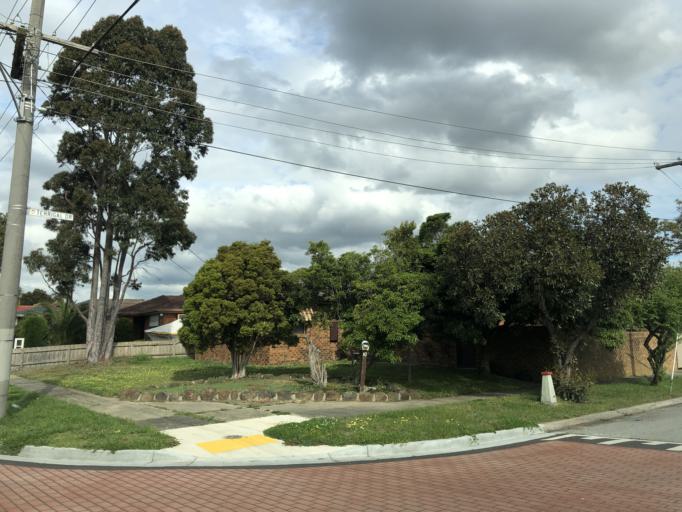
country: AU
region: Victoria
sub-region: Greater Dandenong
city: Noble Park North
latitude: -37.9417
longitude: 145.1933
